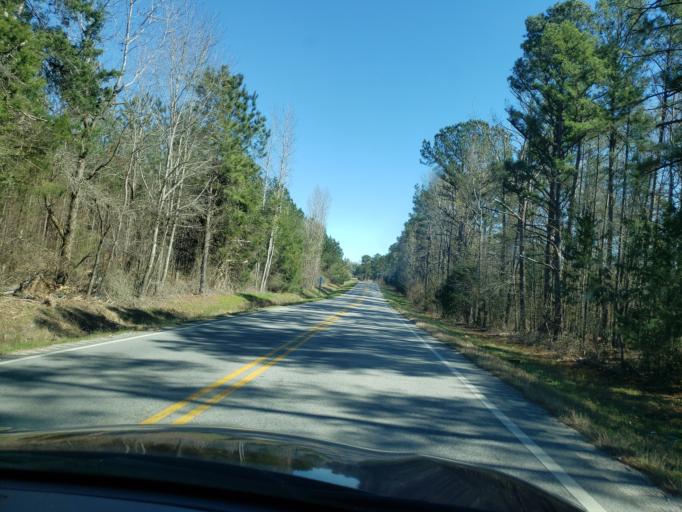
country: US
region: Alabama
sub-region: Lee County
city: Auburn
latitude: 32.5949
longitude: -85.6234
